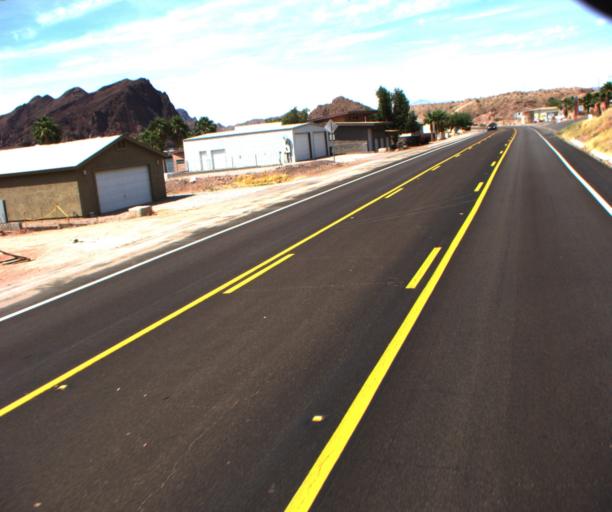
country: US
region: Arizona
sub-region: La Paz County
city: Cienega Springs
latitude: 34.2609
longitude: -114.1294
